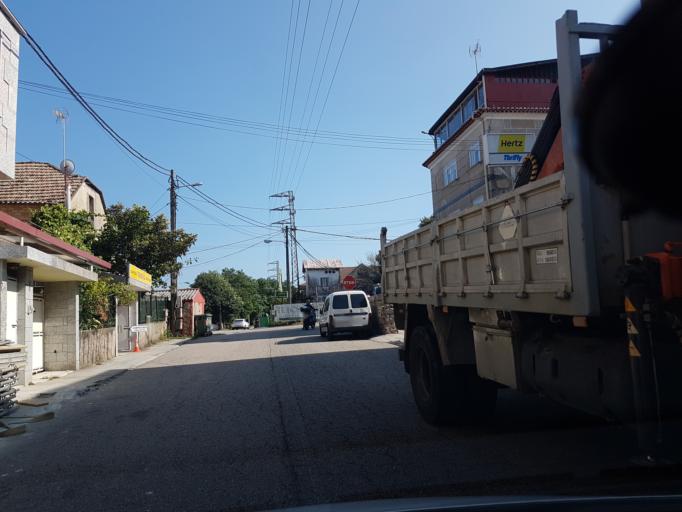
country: ES
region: Galicia
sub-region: Provincia de Pontevedra
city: Porrino
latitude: 42.2214
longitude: -8.6340
